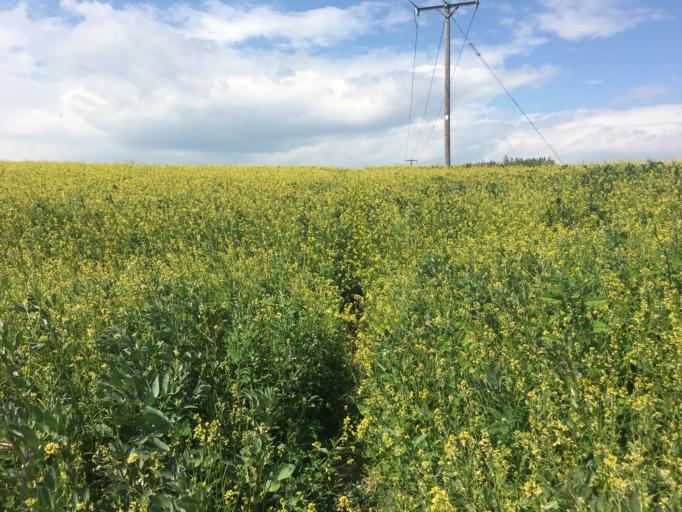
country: GB
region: England
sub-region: Northumberland
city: Belford
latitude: 55.5982
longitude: -1.7964
